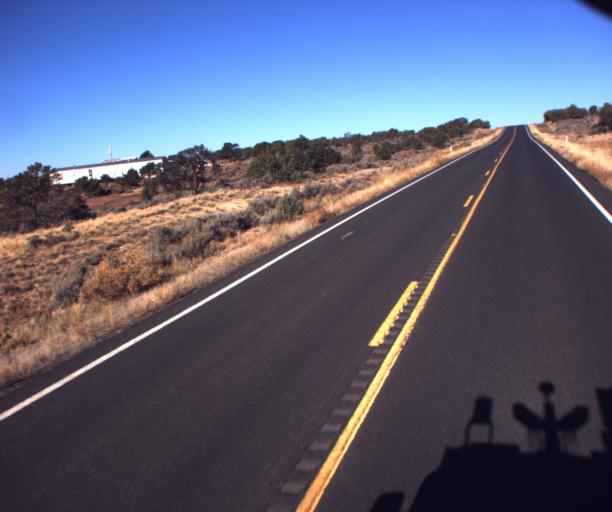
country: US
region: Arizona
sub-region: Apache County
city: Ganado
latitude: 35.7629
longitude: -109.7851
